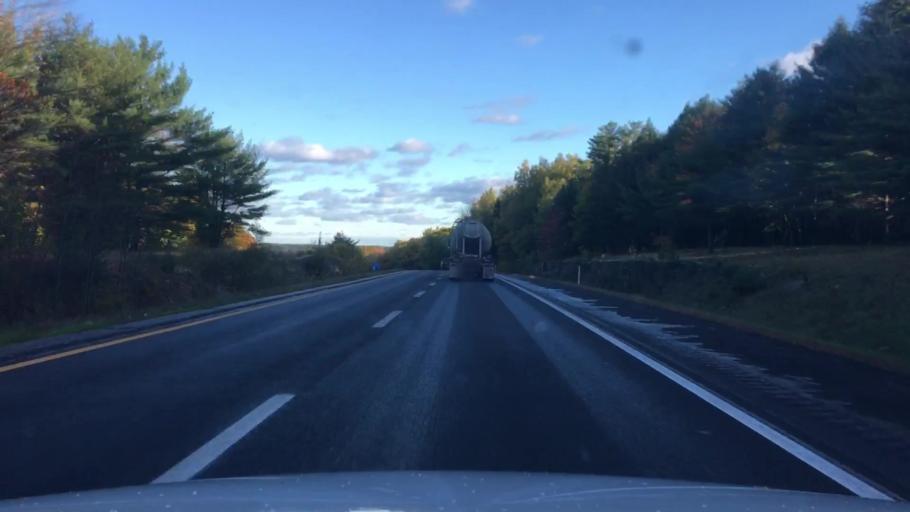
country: US
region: Maine
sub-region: Penobscot County
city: Orono
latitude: 44.8930
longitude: -68.6916
